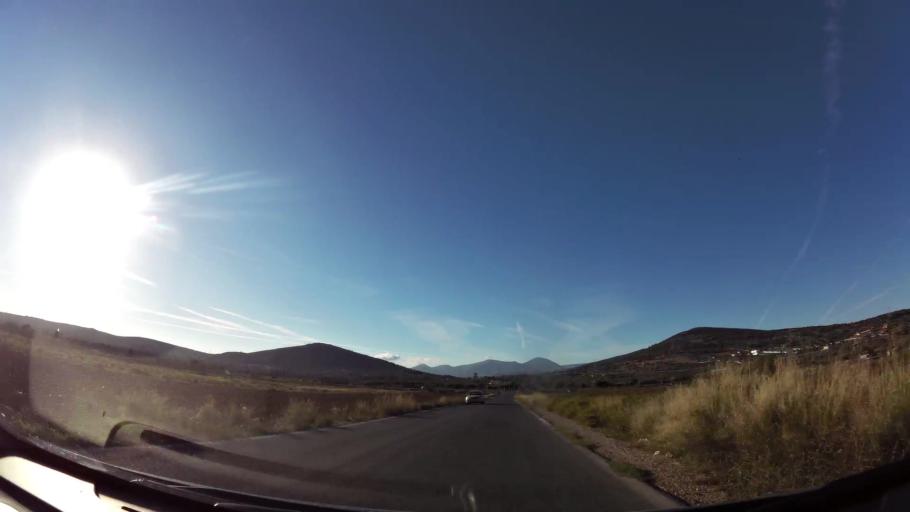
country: GR
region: Attica
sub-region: Nomarchia Anatolikis Attikis
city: Kalyvia Thorikou
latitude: 37.8485
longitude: 23.9163
